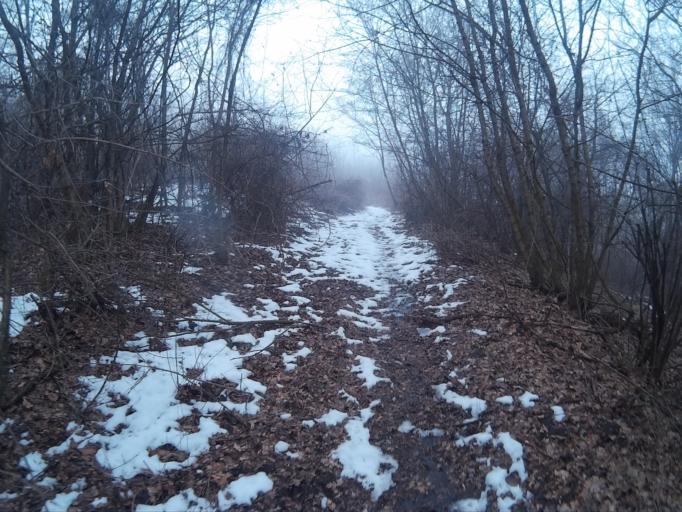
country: HU
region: Nograd
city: Matraverebely
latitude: 47.9805
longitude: 19.7631
